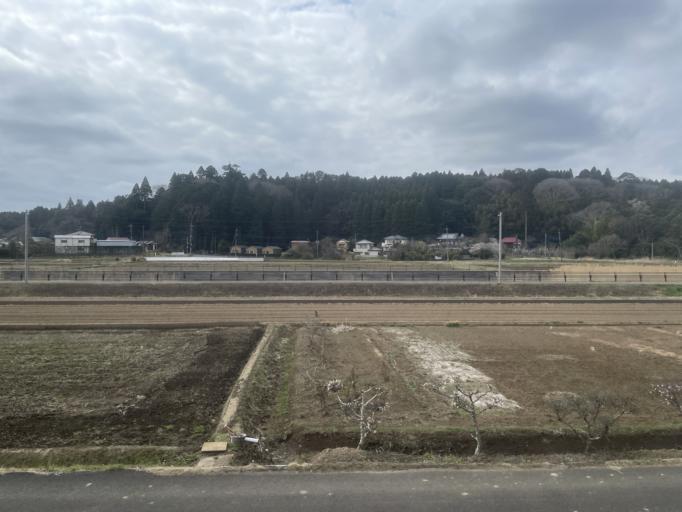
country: JP
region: Chiba
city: Naruto
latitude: 35.6234
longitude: 140.3709
